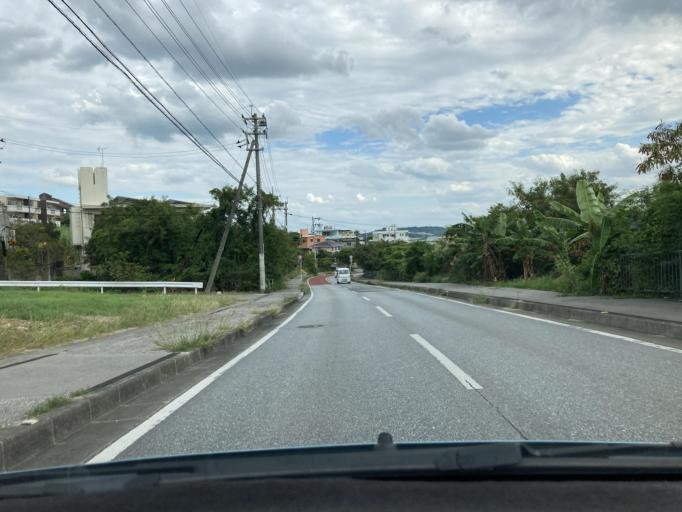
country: JP
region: Okinawa
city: Gushikawa
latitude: 26.3503
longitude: 127.8415
